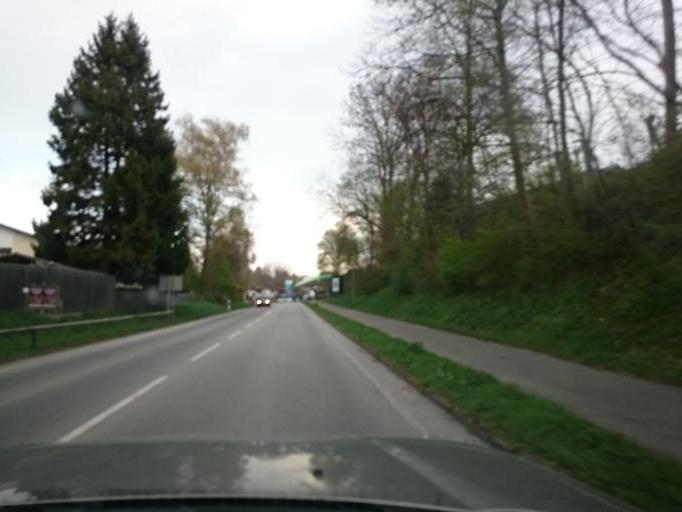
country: DE
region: Bavaria
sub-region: Upper Bavaria
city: Murnau am Staffelsee
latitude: 47.6712
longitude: 11.2003
